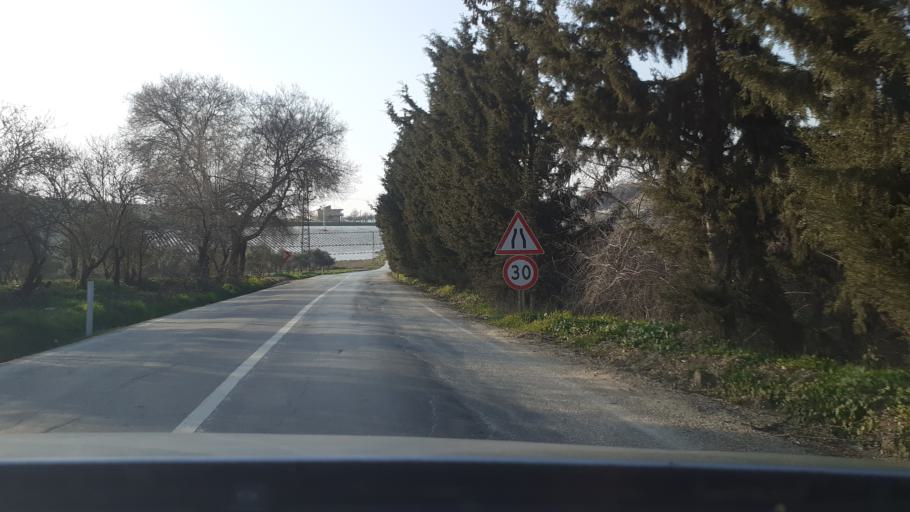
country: TR
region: Hatay
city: Fatikli
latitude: 36.1094
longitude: 36.2726
